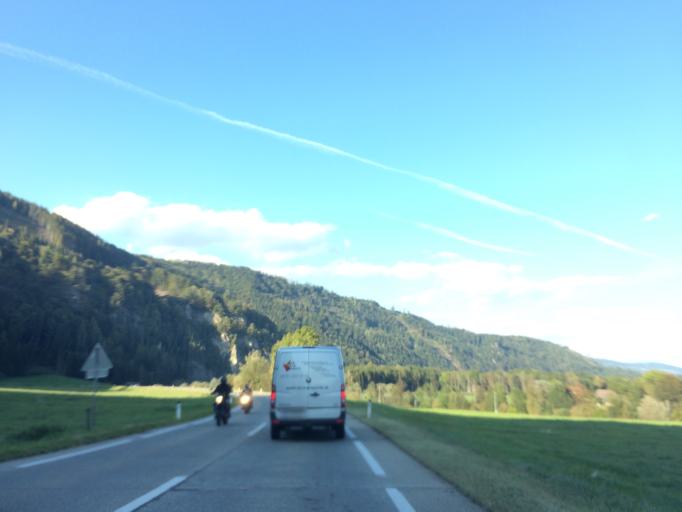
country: AT
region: Styria
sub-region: Politischer Bezirk Leoben
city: Leoben
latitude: 47.3468
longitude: 15.0514
